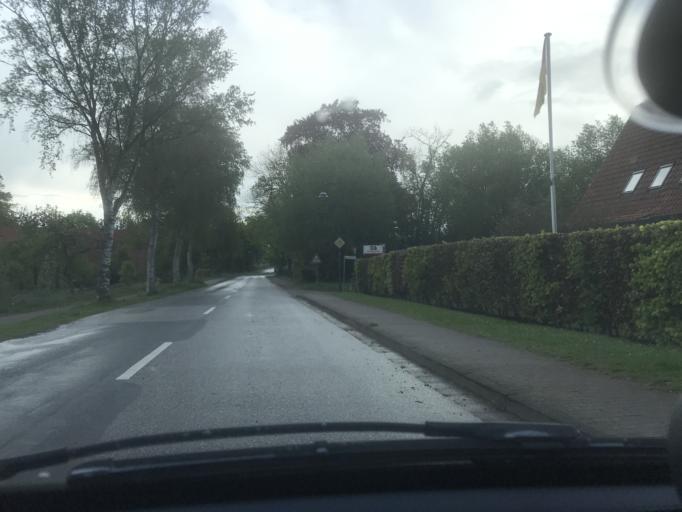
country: DE
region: Lower Saxony
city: Buxtehude
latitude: 53.4516
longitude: 9.6621
